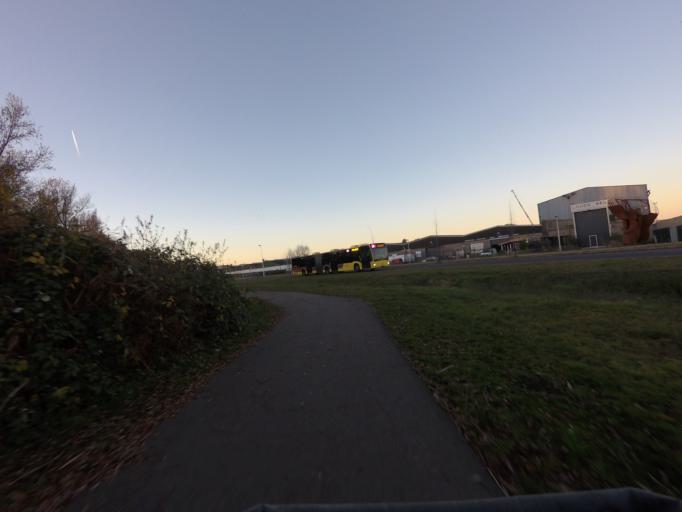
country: NL
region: Utrecht
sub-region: Gemeente Nieuwegein
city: Nieuwegein
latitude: 52.0781
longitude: 5.0610
